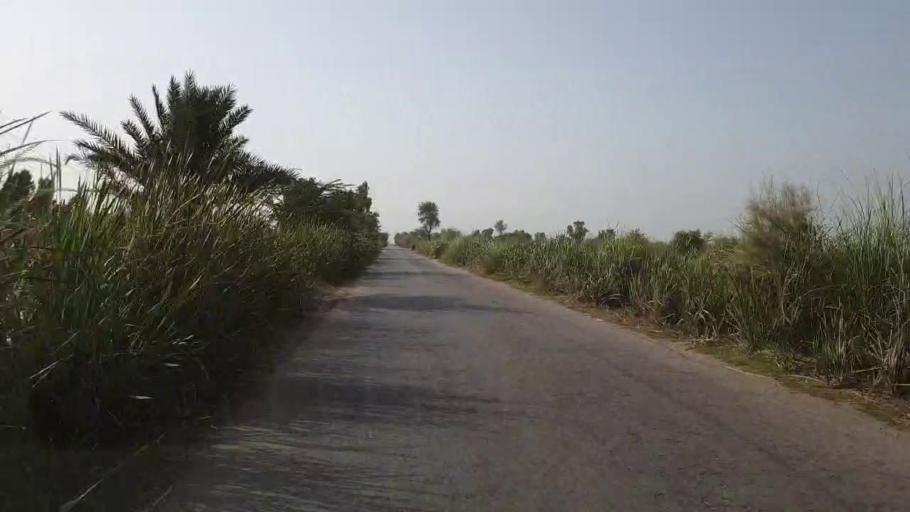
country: PK
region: Sindh
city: Khadro
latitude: 26.3331
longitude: 68.9290
